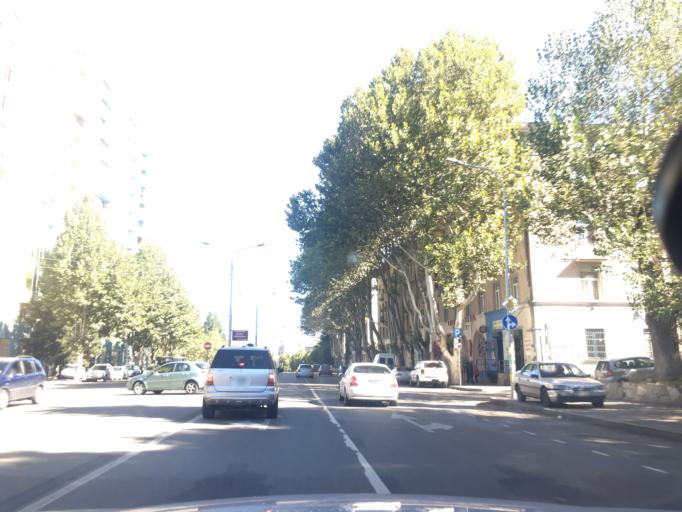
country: GE
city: Zahesi
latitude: 41.7718
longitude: 44.7936
